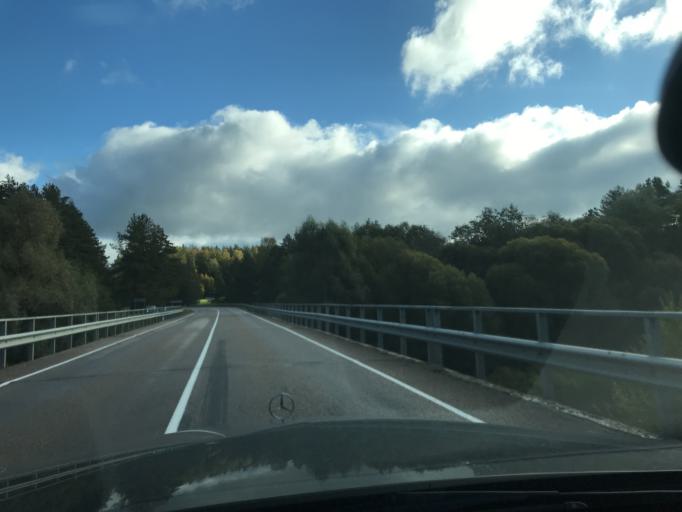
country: EE
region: Valgamaa
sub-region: Torva linn
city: Torva
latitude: 57.9857
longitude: 26.0470
